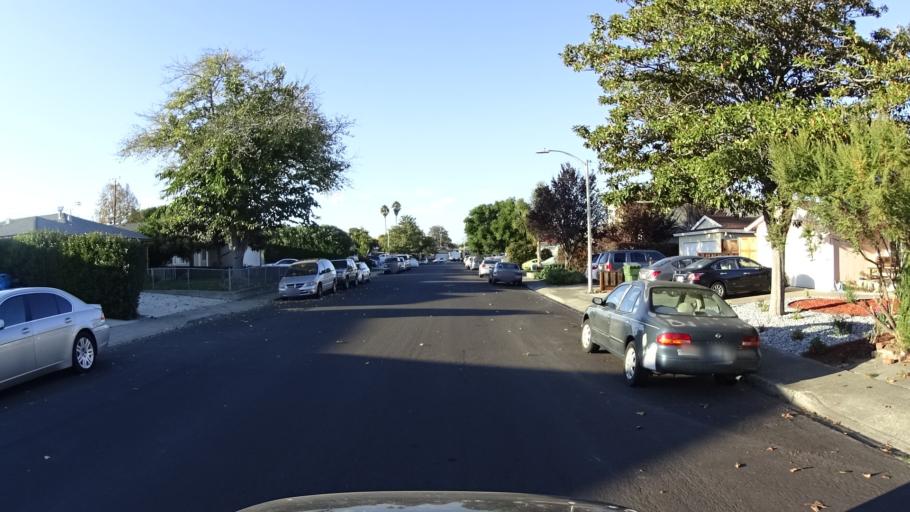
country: US
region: California
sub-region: Santa Clara County
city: Santa Clara
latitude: 37.3636
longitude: -121.9802
